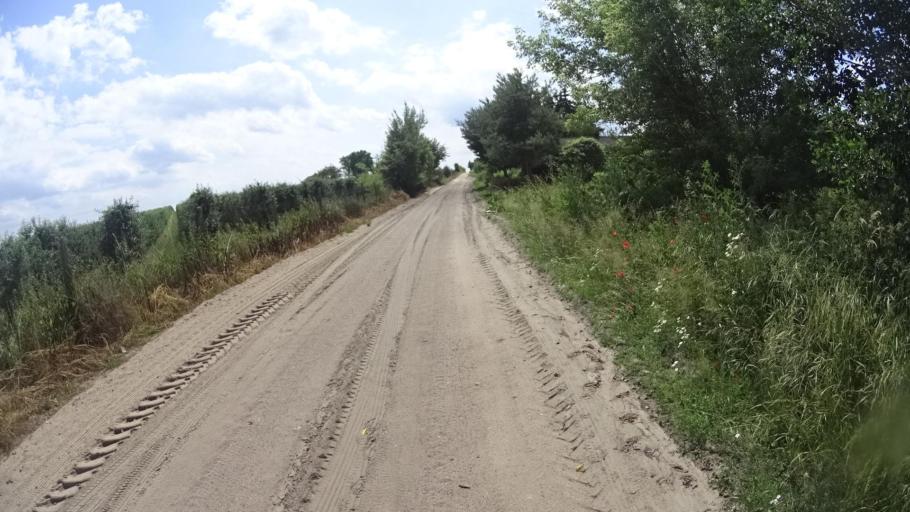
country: PL
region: Masovian Voivodeship
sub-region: Powiat grojecki
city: Goszczyn
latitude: 51.7120
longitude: 20.8316
